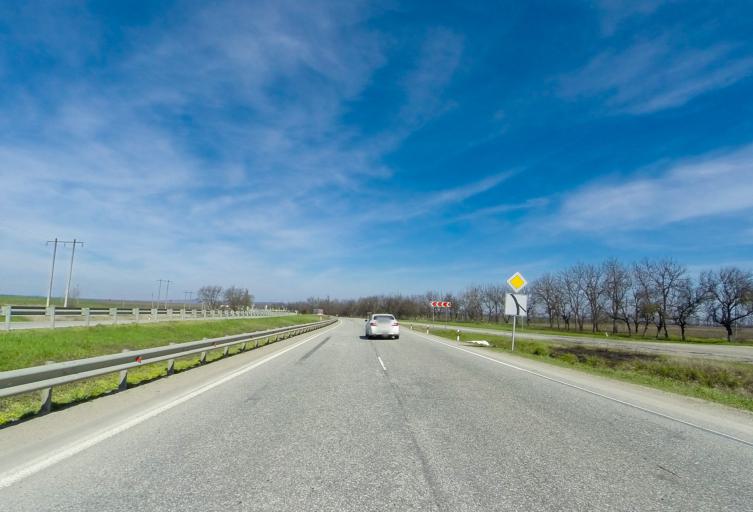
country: RU
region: Kabardino-Balkariya
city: Baksan
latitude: 43.7264
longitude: 43.5165
